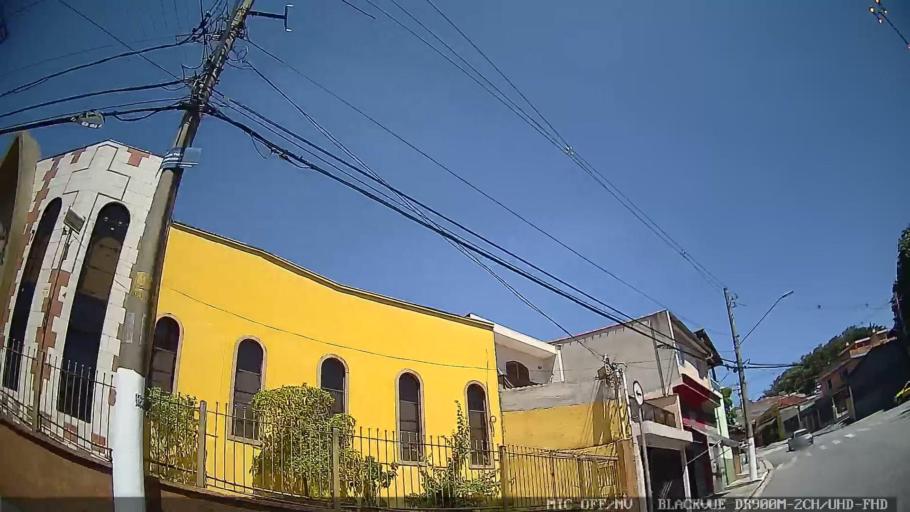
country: BR
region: Sao Paulo
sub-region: Sao Caetano Do Sul
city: Sao Caetano do Sul
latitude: -23.5898
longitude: -46.5308
